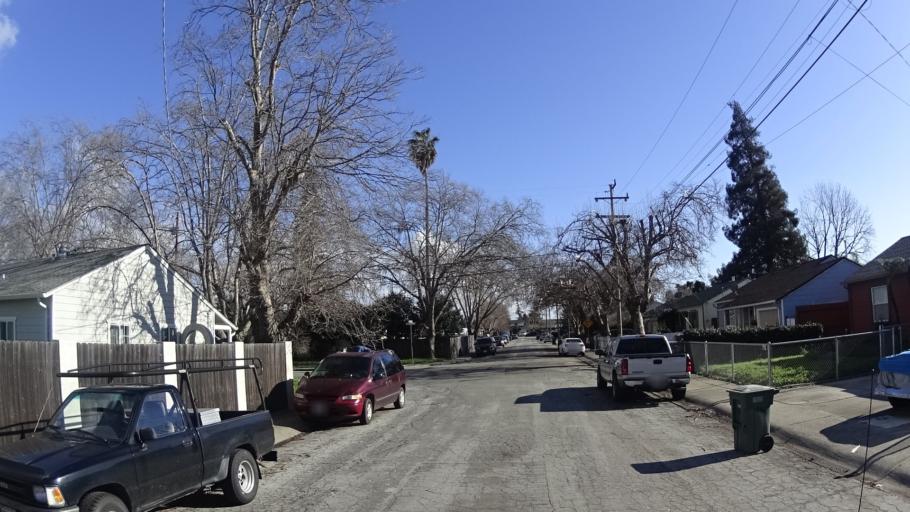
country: US
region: California
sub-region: Alameda County
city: San Lorenzo
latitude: 37.6804
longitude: -122.1151
